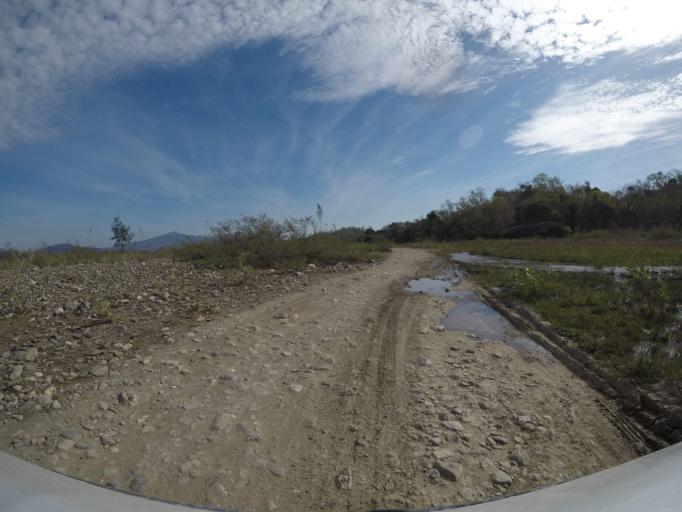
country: TL
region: Bobonaro
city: Maliana
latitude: -8.9008
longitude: 125.2089
